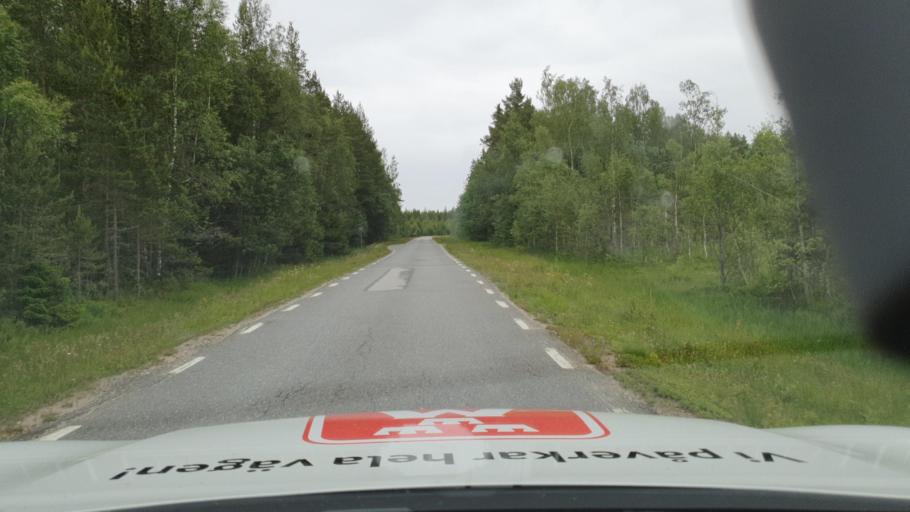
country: SE
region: Vaesterbotten
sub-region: Nordmalings Kommun
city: Nordmaling
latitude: 63.4332
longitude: 19.4791
